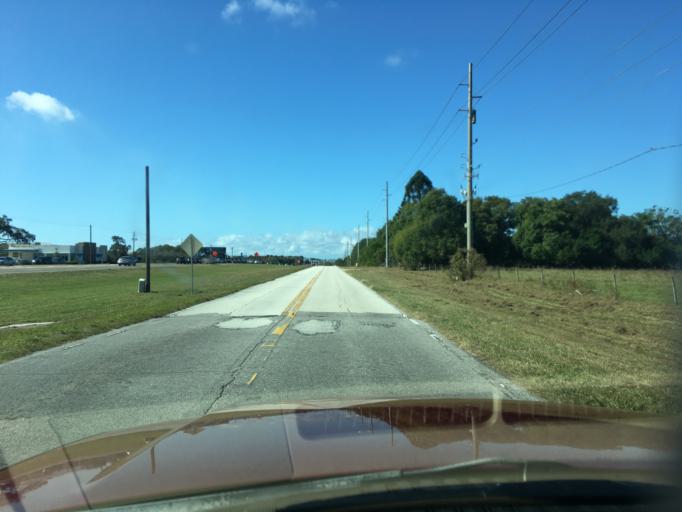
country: US
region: Florida
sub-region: Hillsborough County
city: Apollo Beach
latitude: 27.7920
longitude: -82.3433
